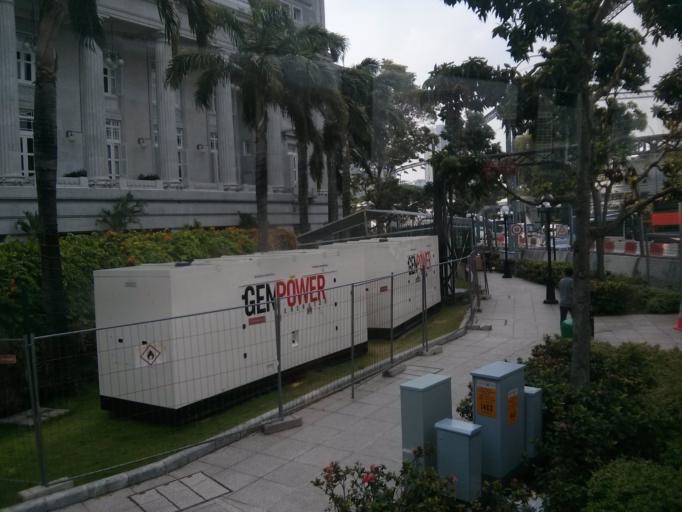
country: SG
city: Singapore
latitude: 1.2860
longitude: 103.8533
